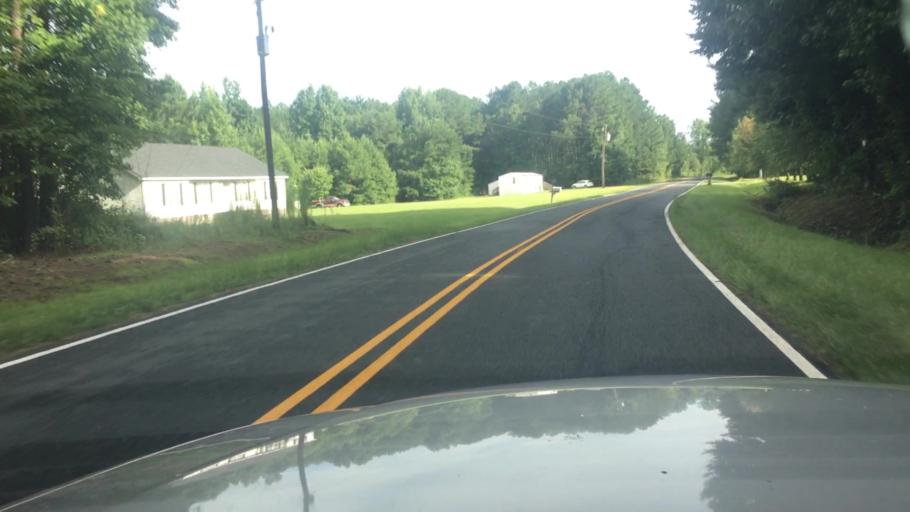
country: US
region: North Carolina
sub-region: Cumberland County
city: Eastover
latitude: 35.1589
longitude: -78.8536
